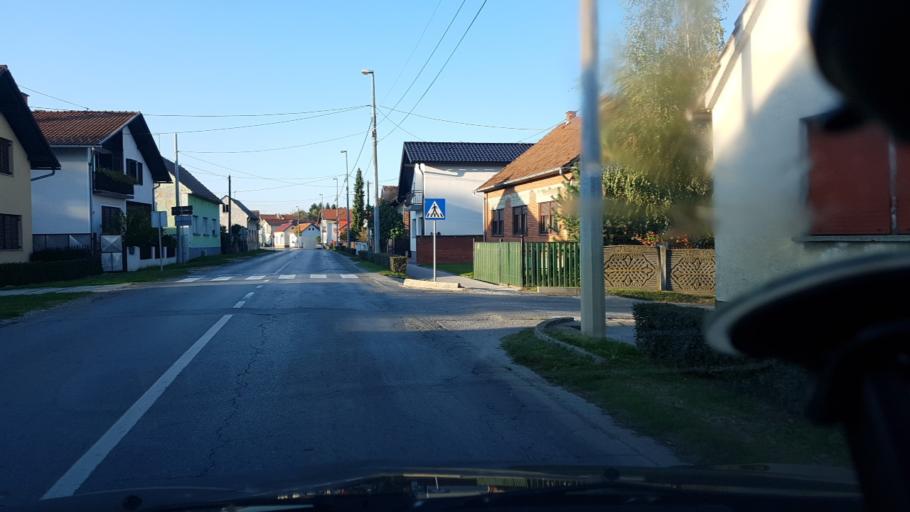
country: HR
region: Koprivnicko-Krizevacka
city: Kalinovac
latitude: 46.0421
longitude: 17.0579
